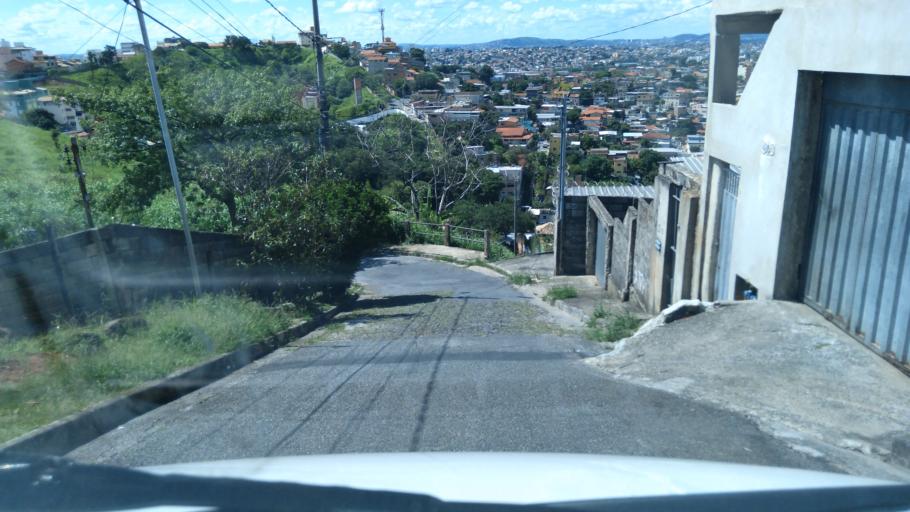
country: BR
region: Minas Gerais
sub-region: Belo Horizonte
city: Belo Horizonte
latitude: -19.8728
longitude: -43.9124
